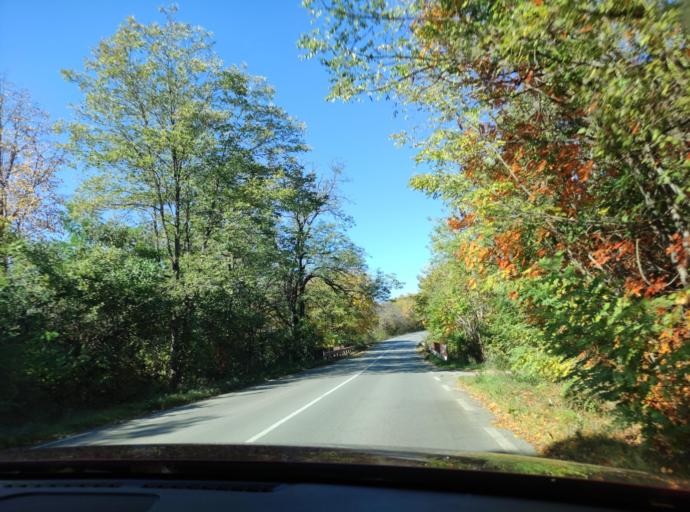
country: BG
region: Montana
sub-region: Obshtina Montana
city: Montana
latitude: 43.3999
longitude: 23.0931
